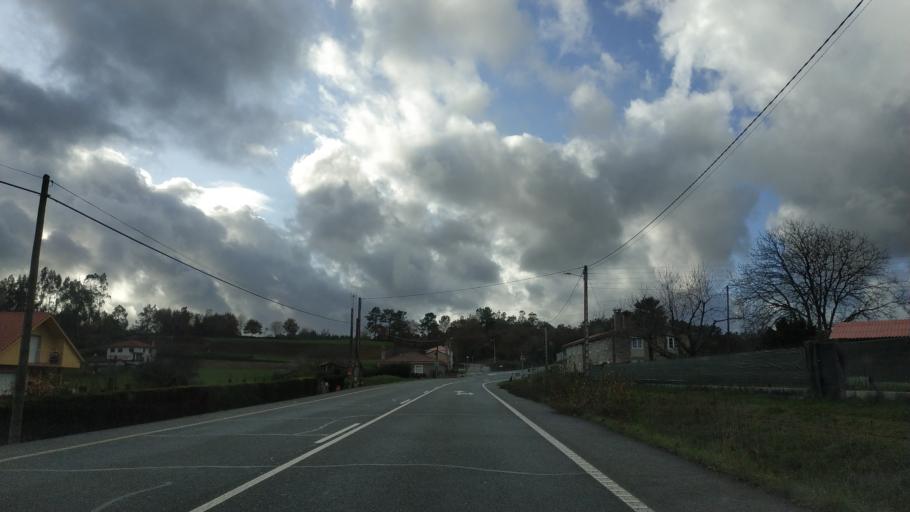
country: ES
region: Galicia
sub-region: Provincia da Coruna
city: Arzua
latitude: 42.8829
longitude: -8.1912
